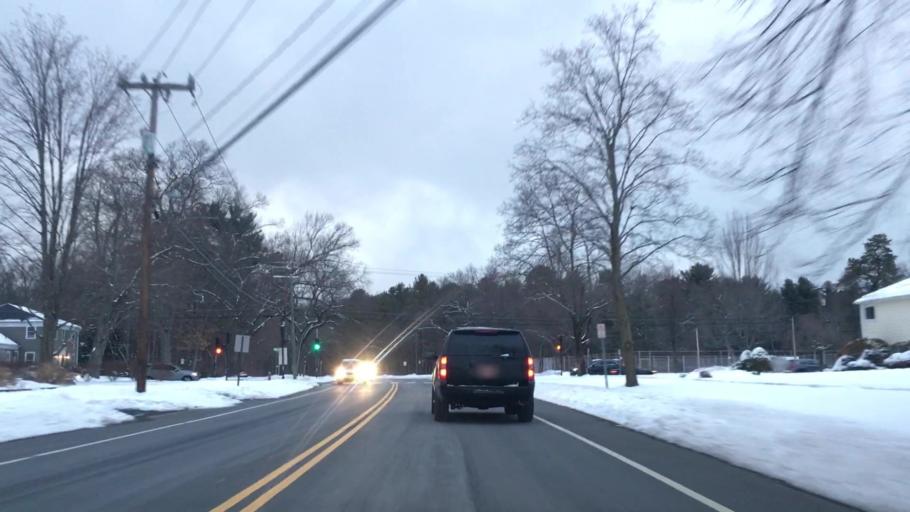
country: US
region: Massachusetts
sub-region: Hampden County
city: Longmeadow
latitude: 42.0568
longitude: -72.5719
